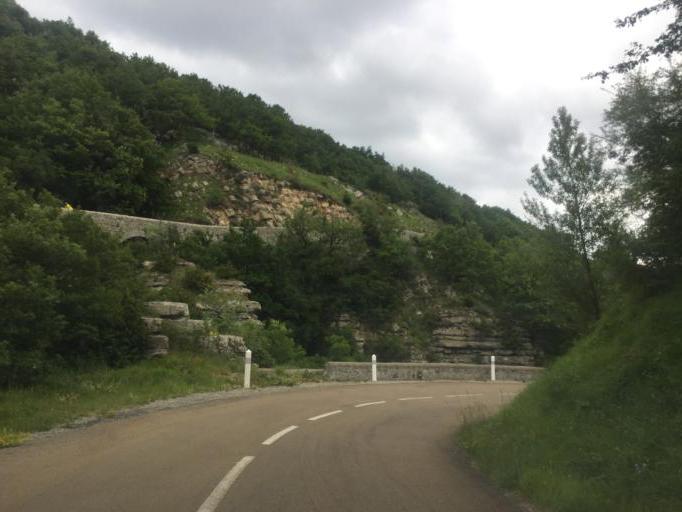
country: FR
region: Rhone-Alpes
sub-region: Departement de l'Ardeche
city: Saint-Priest
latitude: 44.6979
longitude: 4.5600
